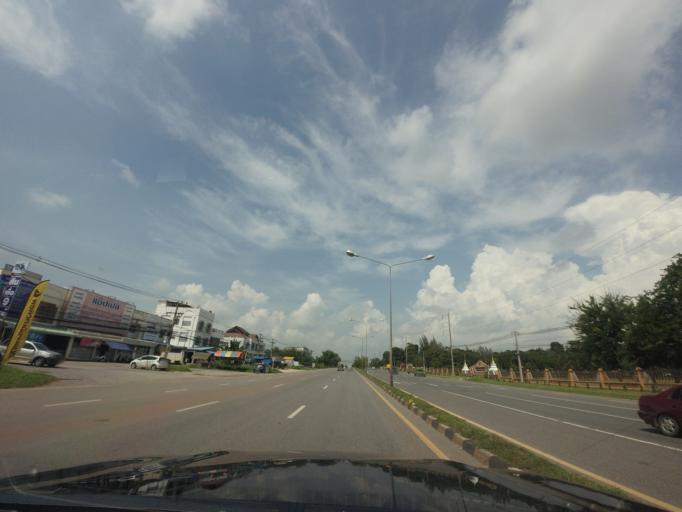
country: TH
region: Khon Kaen
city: Ban Fang
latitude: 16.4503
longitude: 102.7276
